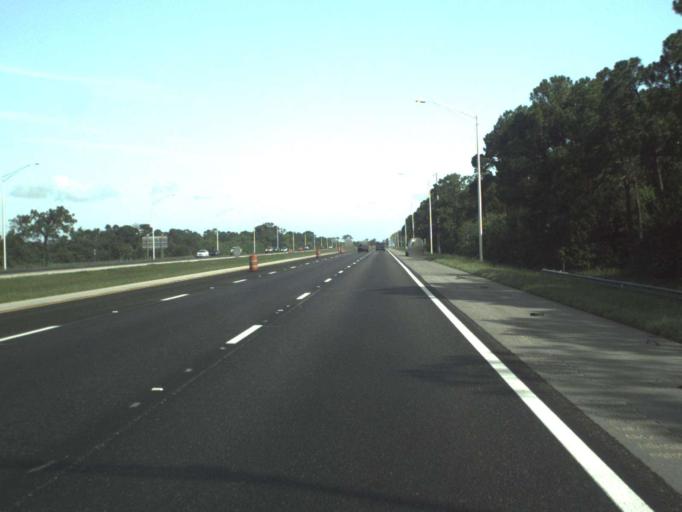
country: US
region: Florida
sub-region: Indian River County
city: West Vero Corridor
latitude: 27.5619
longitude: -80.4835
